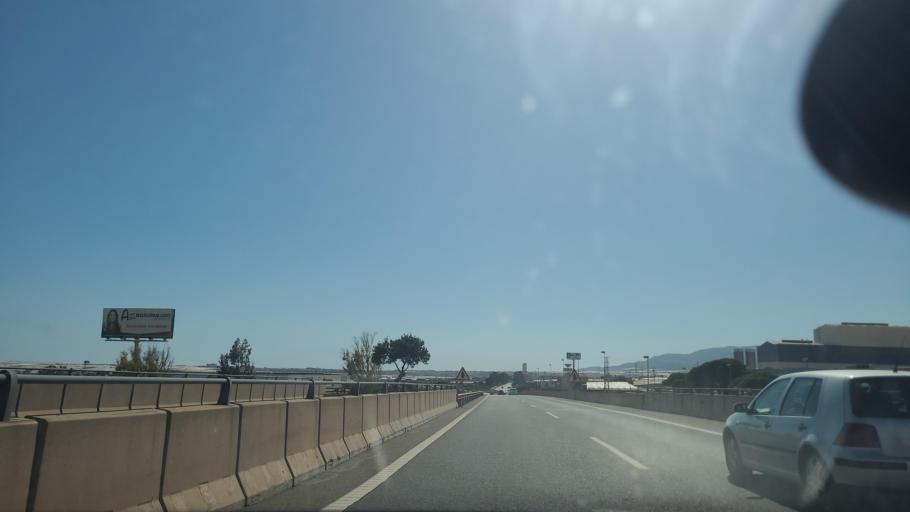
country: ES
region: Andalusia
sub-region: Provincia de Almeria
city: El Ejido
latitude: 36.7842
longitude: -2.7503
